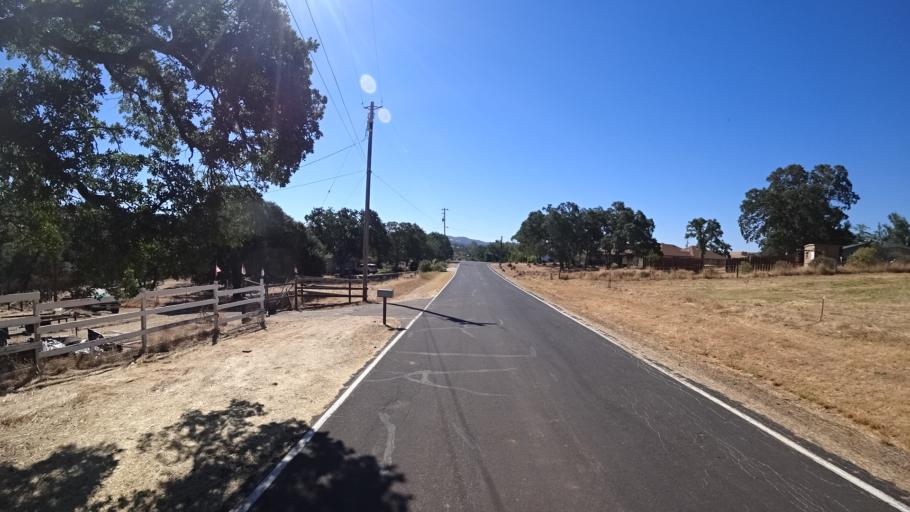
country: US
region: California
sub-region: Calaveras County
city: Rancho Calaveras
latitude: 38.0962
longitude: -120.8559
